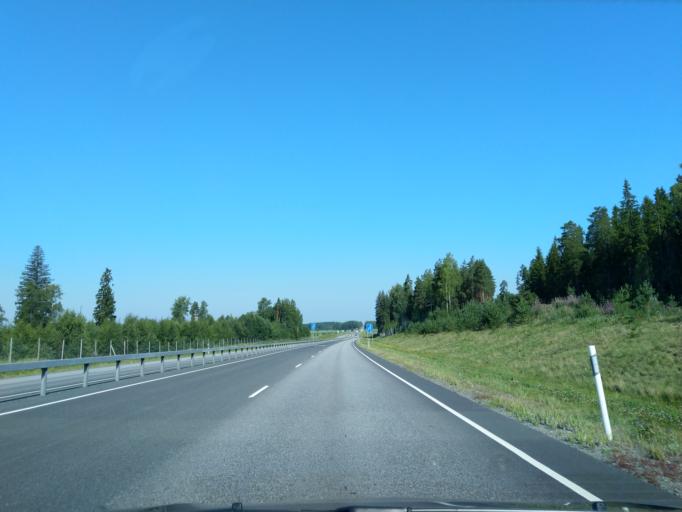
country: FI
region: Varsinais-Suomi
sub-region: Loimaa
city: Alastaro
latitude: 61.0567
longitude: 22.9476
